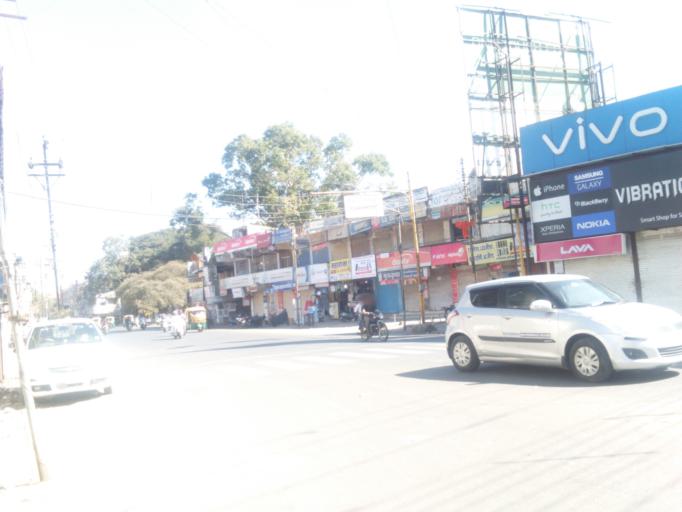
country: IN
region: Madhya Pradesh
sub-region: Indore
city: Indore
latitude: 22.7189
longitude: 75.8628
